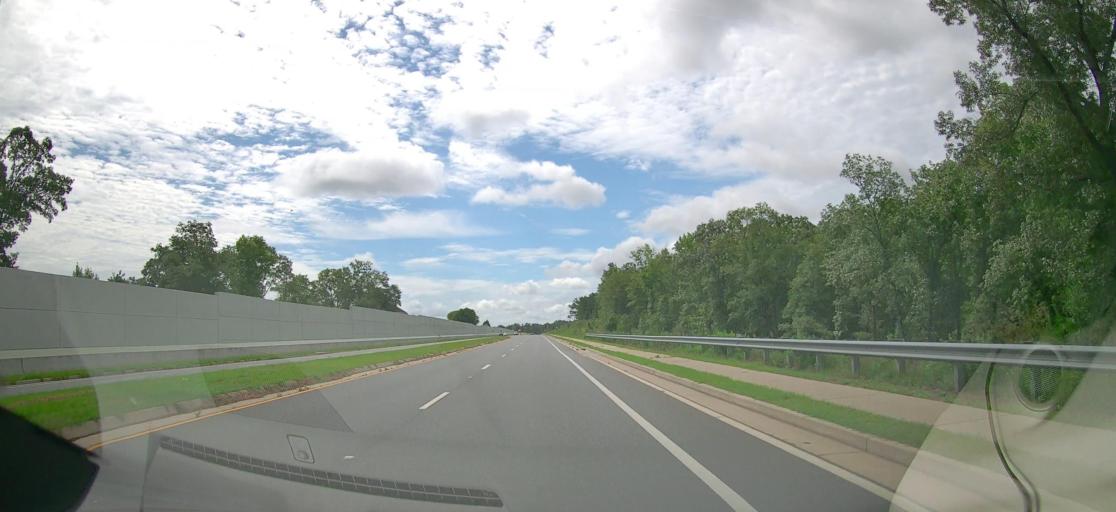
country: US
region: Georgia
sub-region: Peach County
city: Byron
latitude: 32.7150
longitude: -83.7020
